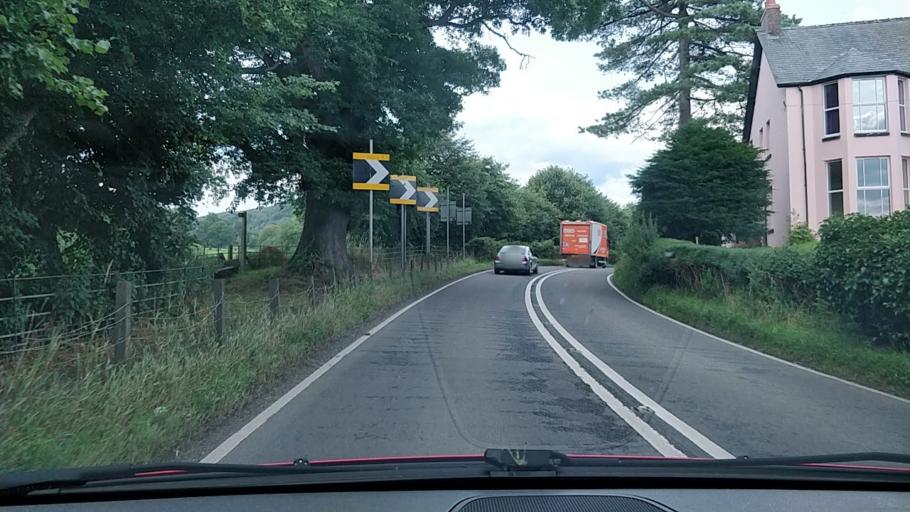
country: GB
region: Wales
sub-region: Gwynedd
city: Bala
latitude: 52.9146
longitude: -3.5911
